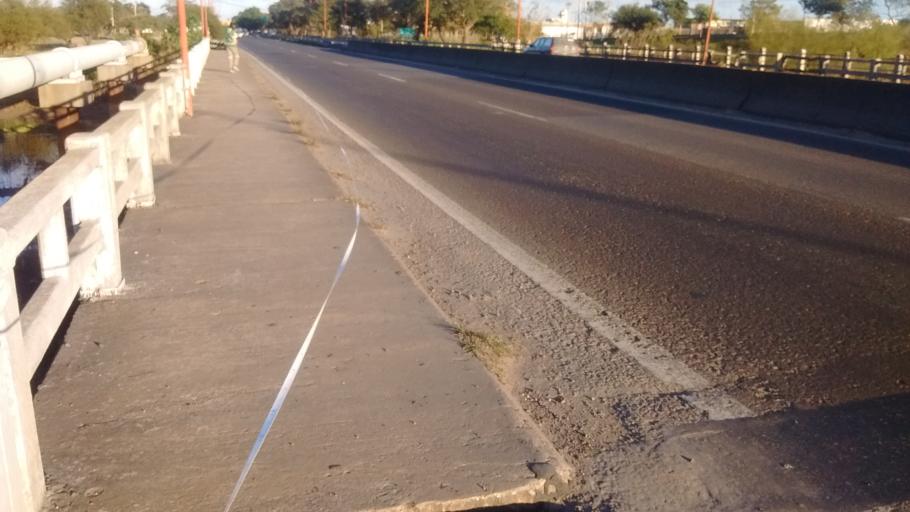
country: AR
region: Santa Fe
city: Santa Fe de la Vera Cruz
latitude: -31.6407
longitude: -60.6650
